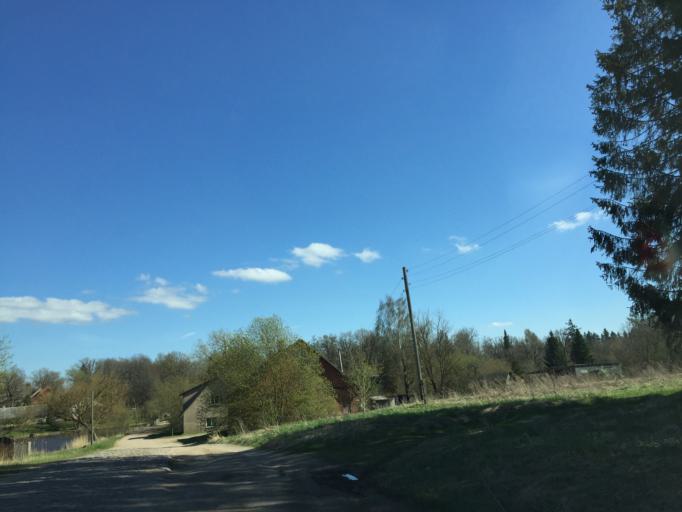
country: EE
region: Valgamaa
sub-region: Valga linn
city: Valga
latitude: 57.8699
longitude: 26.2431
